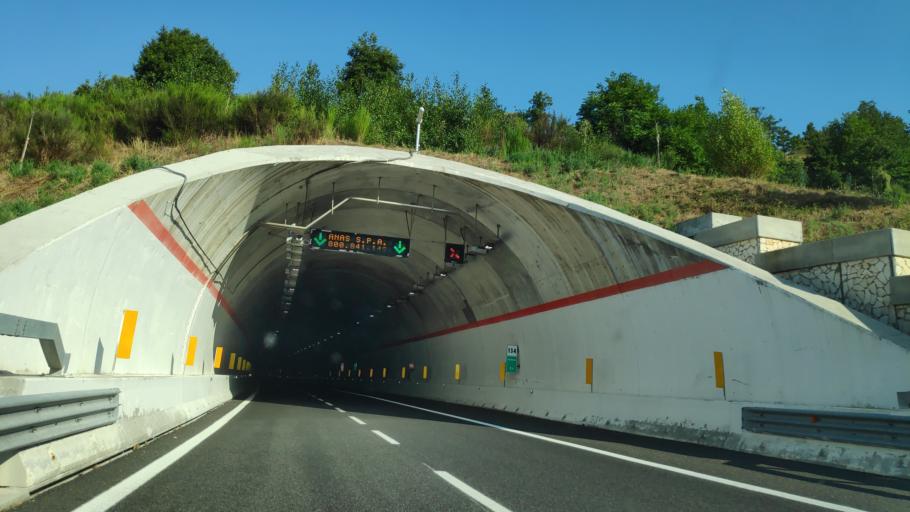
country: IT
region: Basilicate
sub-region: Provincia di Potenza
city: Lagonegro
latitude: 40.1108
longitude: 15.7916
